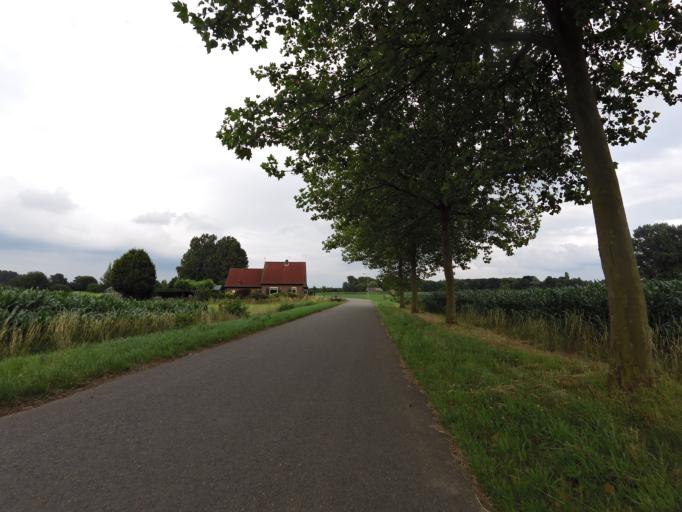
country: NL
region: Gelderland
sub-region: Gemeente Doesburg
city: Doesburg
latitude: 51.9952
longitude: 6.1495
